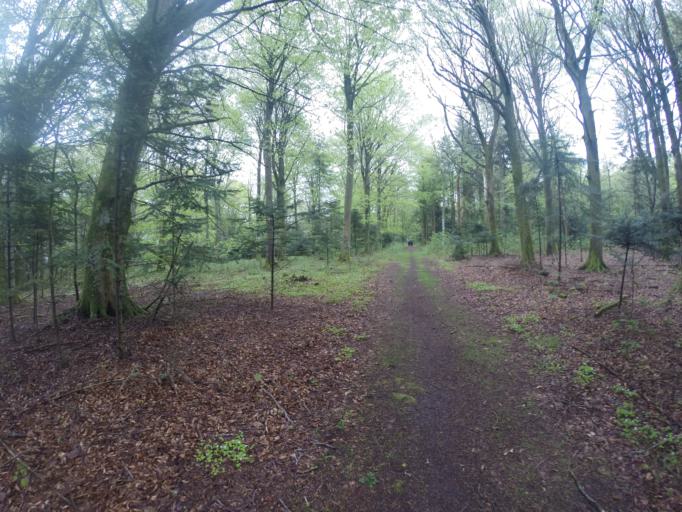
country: DK
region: North Denmark
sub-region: Thisted Kommune
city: Hanstholm
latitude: 57.0309
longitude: 8.5901
